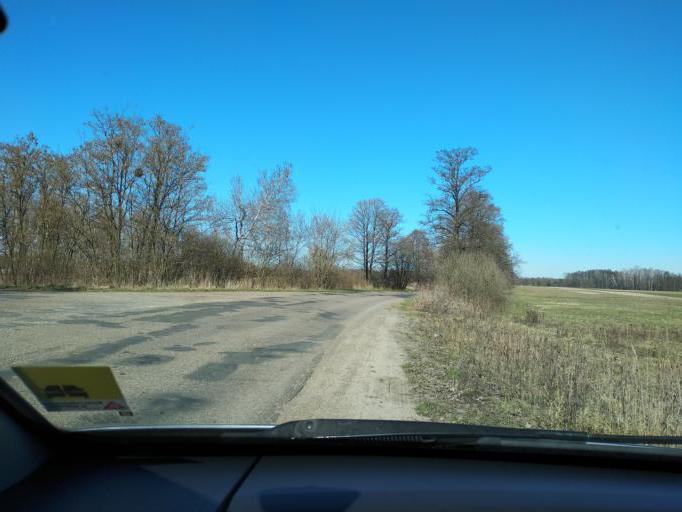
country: PL
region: Lublin Voivodeship
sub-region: Powiat pulawski
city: Kurow
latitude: 51.4159
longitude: 22.2012
